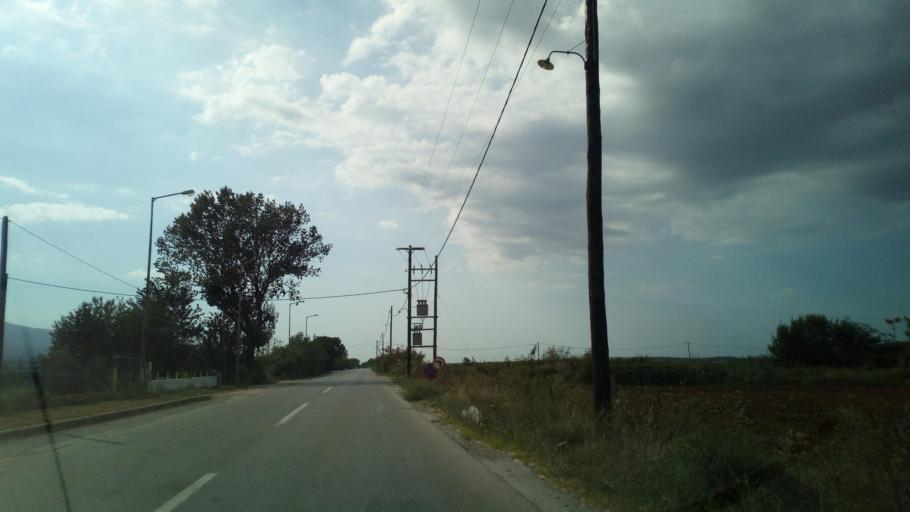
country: GR
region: Central Macedonia
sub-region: Nomos Thessalonikis
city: Gerakarou
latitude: 40.5782
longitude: 23.2726
